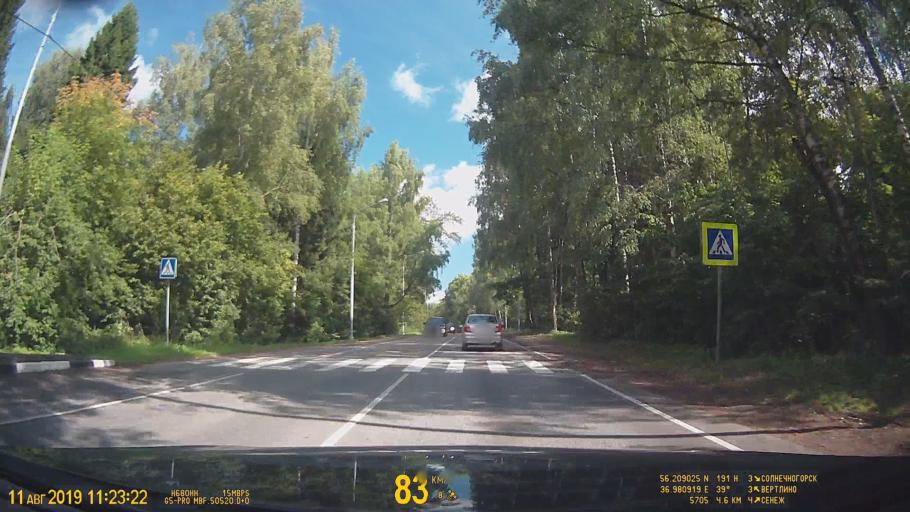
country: RU
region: Moskovskaya
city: Solnechnogorsk
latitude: 56.2093
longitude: 36.9814
